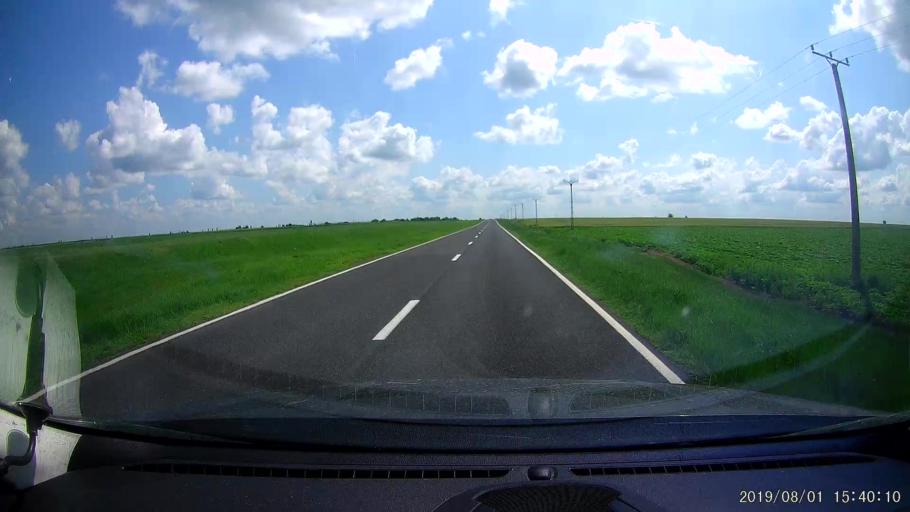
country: RO
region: Braila
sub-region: Comuna Baraganul
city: Baraganul
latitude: 44.8426
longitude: 27.5470
